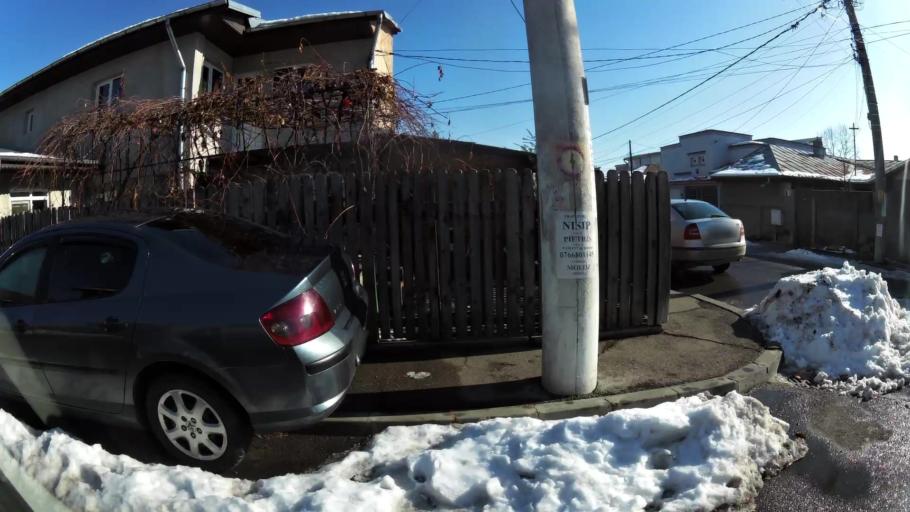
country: RO
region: Ilfov
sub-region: Comuna Magurele
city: Magurele
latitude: 44.3967
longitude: 26.0519
